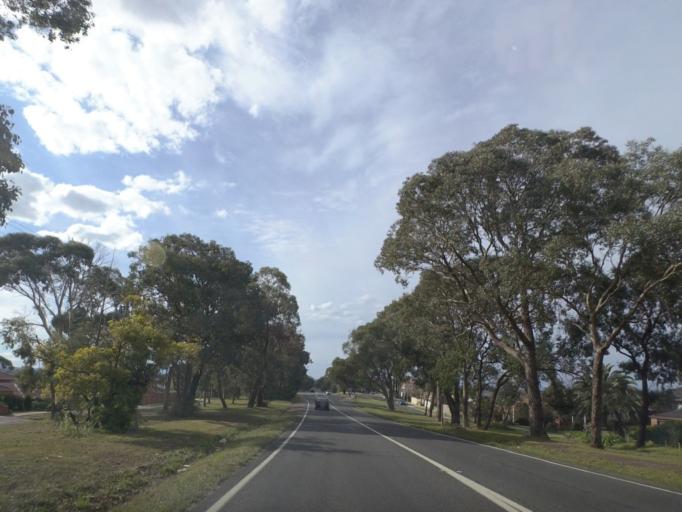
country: AU
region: Victoria
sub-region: Manningham
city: Donvale
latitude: -37.7720
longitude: 145.1700
